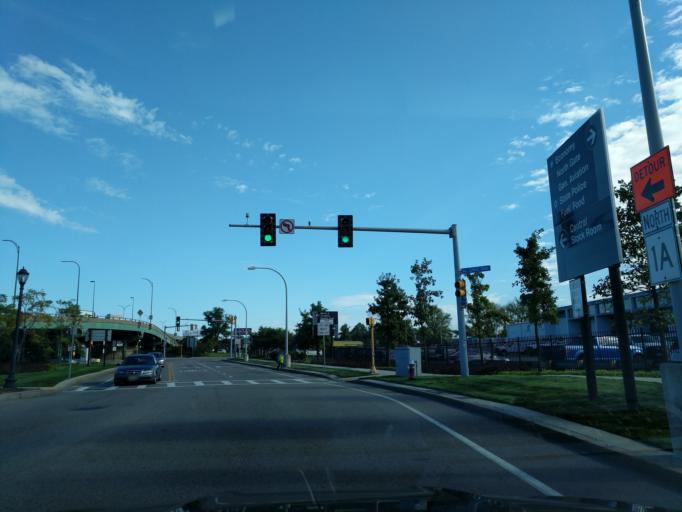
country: US
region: Massachusetts
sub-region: Suffolk County
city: Chelsea
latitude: 42.3776
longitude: -71.0262
